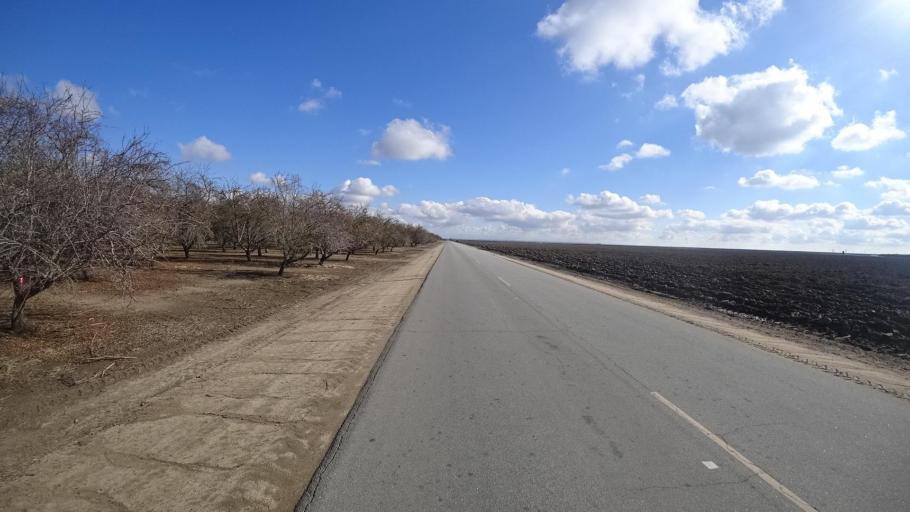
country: US
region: California
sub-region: Kern County
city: McFarland
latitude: 35.6743
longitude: -119.2910
